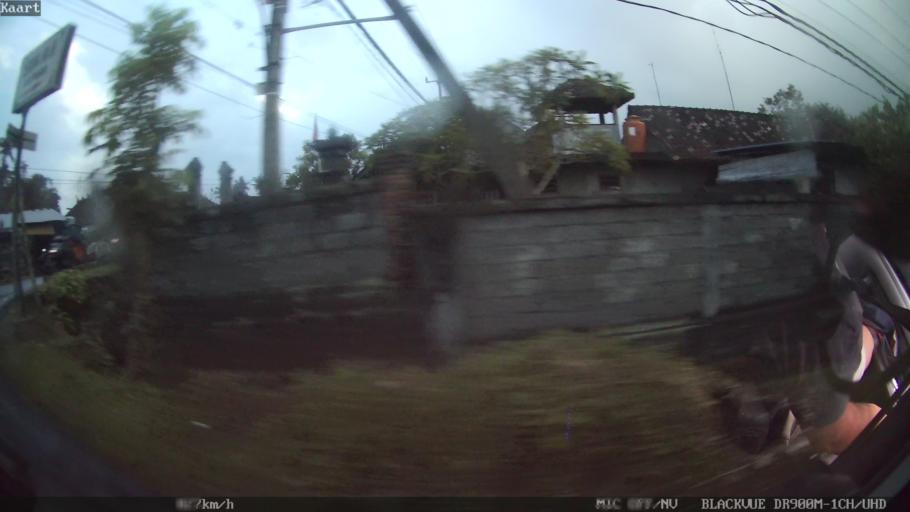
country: ID
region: Bali
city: Banjar Batur
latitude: -8.5988
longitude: 115.2146
